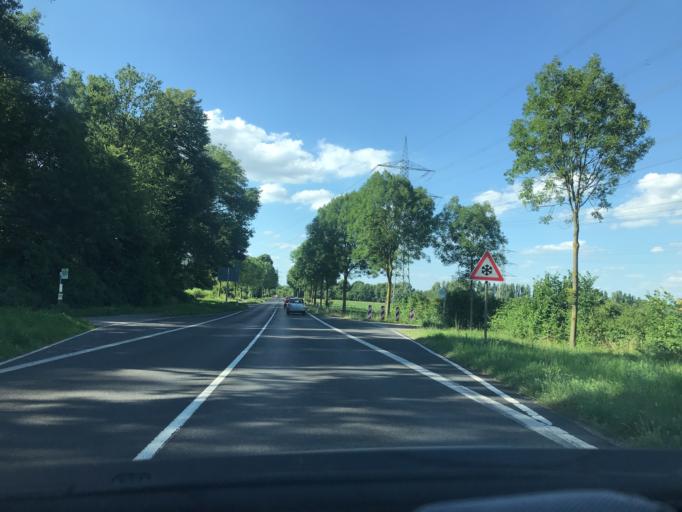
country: DE
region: North Rhine-Westphalia
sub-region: Regierungsbezirk Dusseldorf
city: Neuss
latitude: 51.1560
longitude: 6.6826
